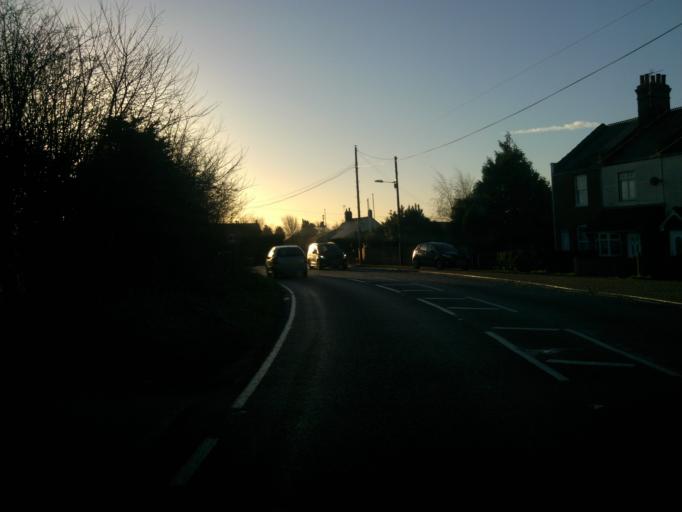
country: GB
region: England
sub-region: Essex
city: Saint Osyth
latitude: 51.8239
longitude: 1.0671
